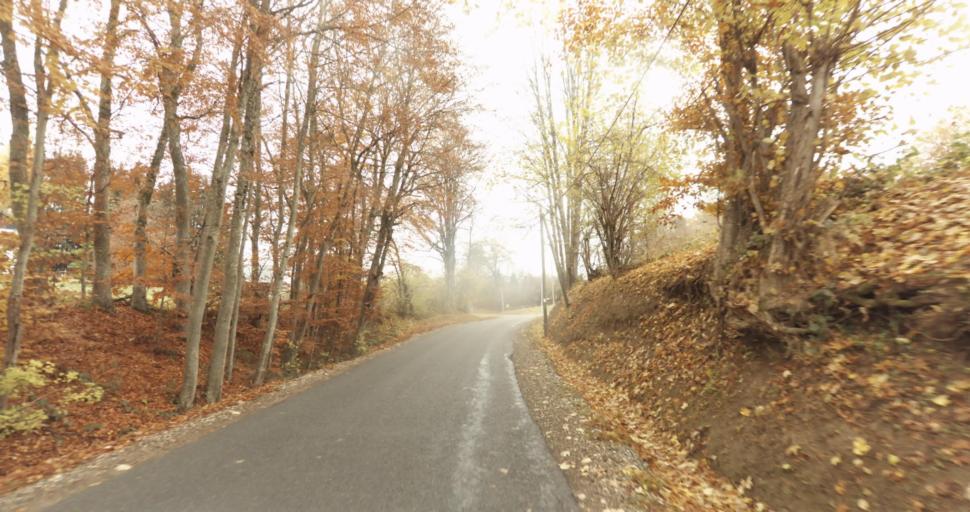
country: FR
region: Rhone-Alpes
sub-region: Departement de la Haute-Savoie
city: Evires
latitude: 46.0566
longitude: 6.2085
